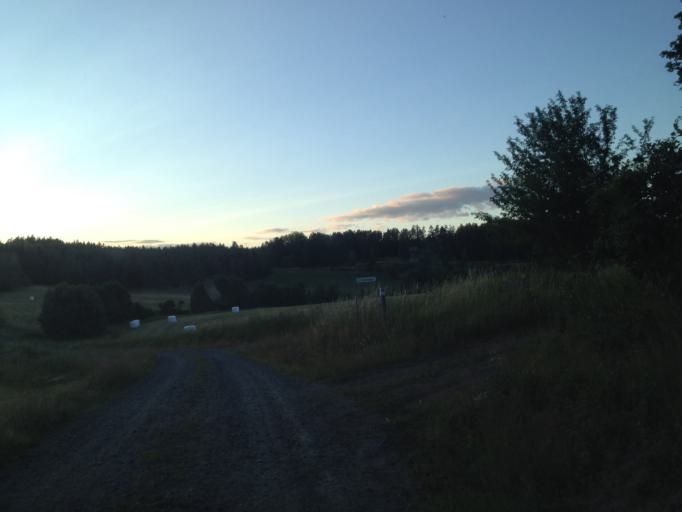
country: SE
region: Kalmar
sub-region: Vasterviks Kommun
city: Overum
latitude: 58.0195
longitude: 16.1206
